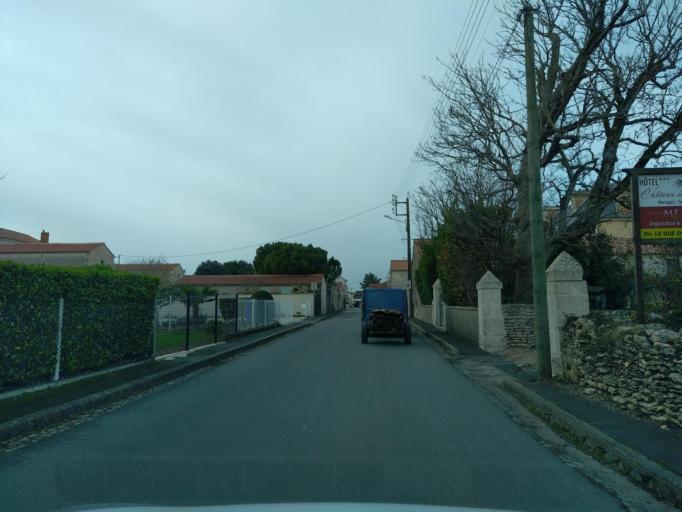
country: FR
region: Pays de la Loire
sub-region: Departement de la Vendee
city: Vix
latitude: 46.3612
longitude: -0.8551
